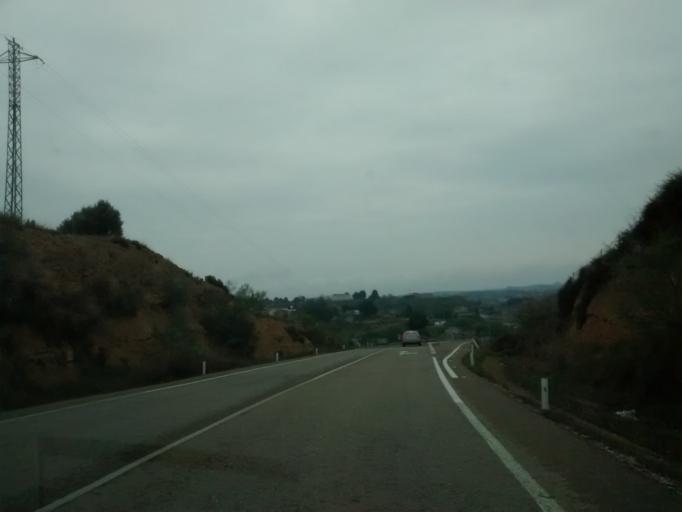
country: ES
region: Aragon
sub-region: Provincia de Zaragoza
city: Caspe
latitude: 41.2373
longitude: -0.0564
